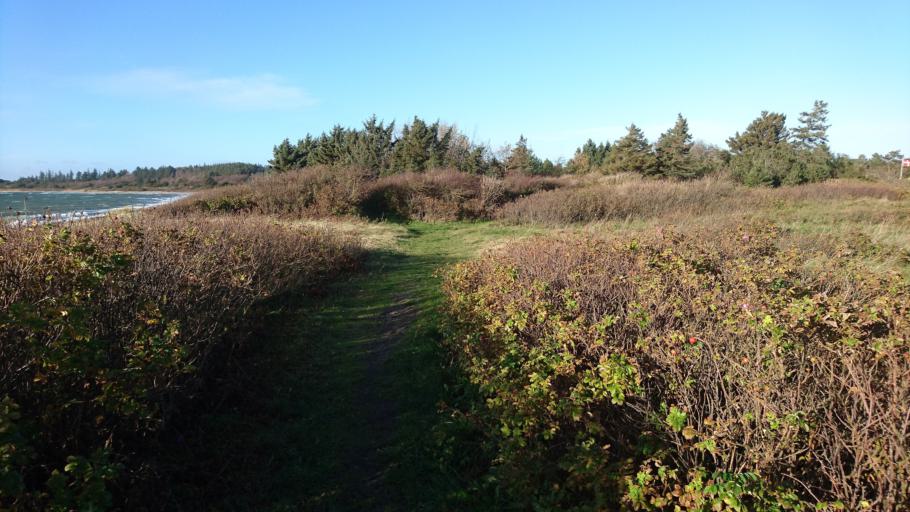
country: DK
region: North Denmark
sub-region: Morso Kommune
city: Nykobing Mors
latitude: 56.8270
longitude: 8.9663
